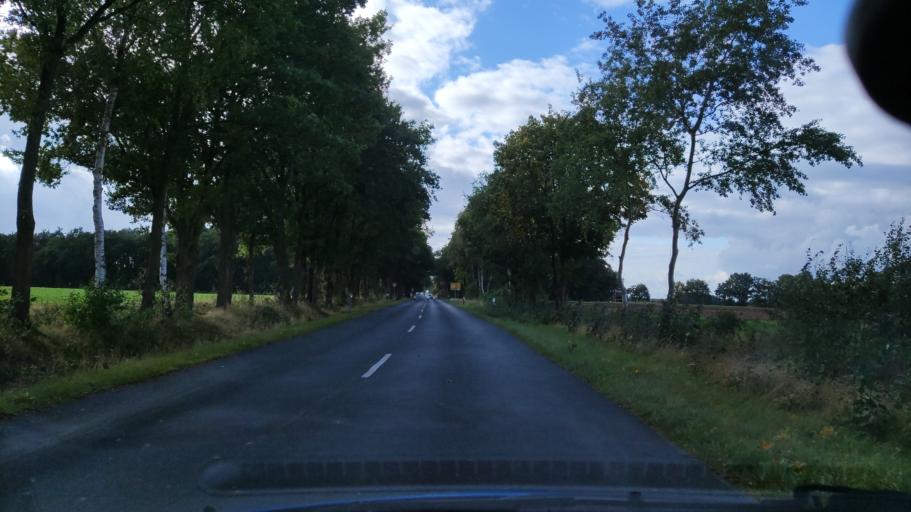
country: DE
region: Lower Saxony
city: Wendisch Evern
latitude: 53.2074
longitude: 10.4526
